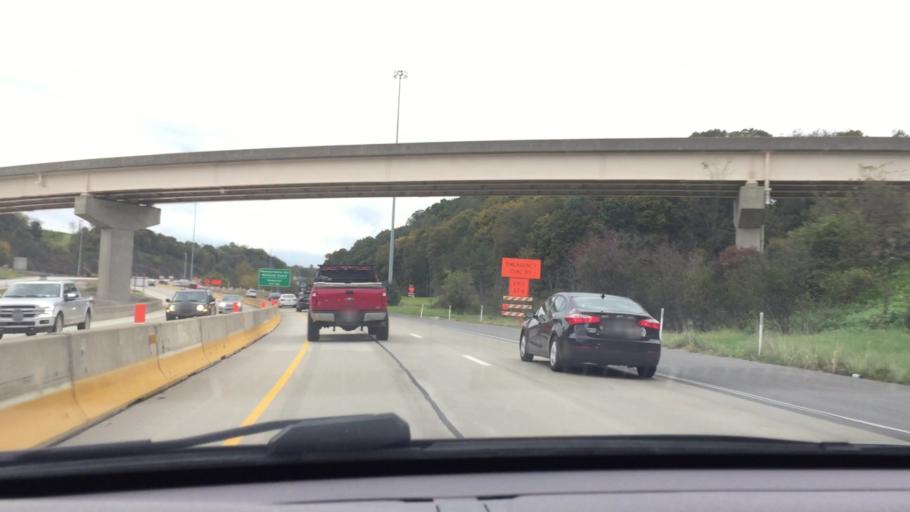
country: US
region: Pennsylvania
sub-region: Allegheny County
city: Enlow
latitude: 40.4678
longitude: -80.1988
